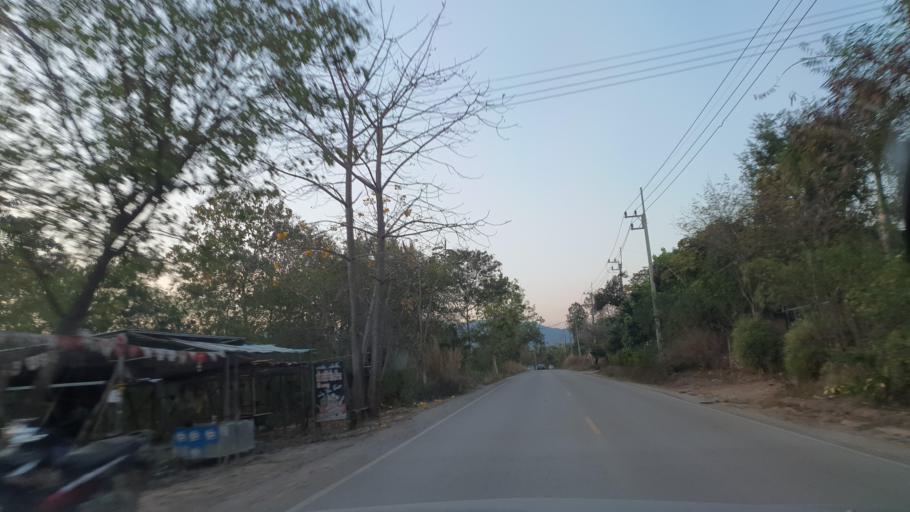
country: TH
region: Chiang Mai
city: Mae Wang
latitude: 18.6359
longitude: 98.8001
